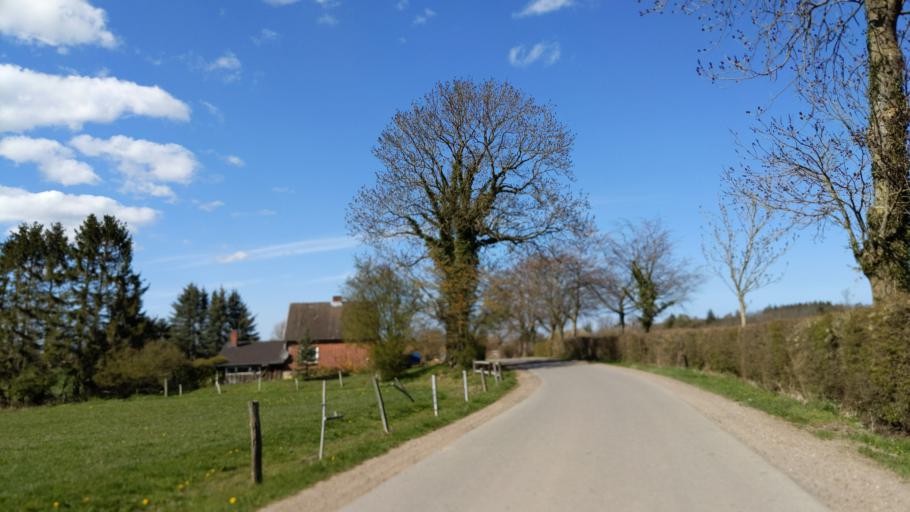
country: DE
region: Schleswig-Holstein
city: Kasseedorf
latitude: 54.1311
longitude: 10.6909
